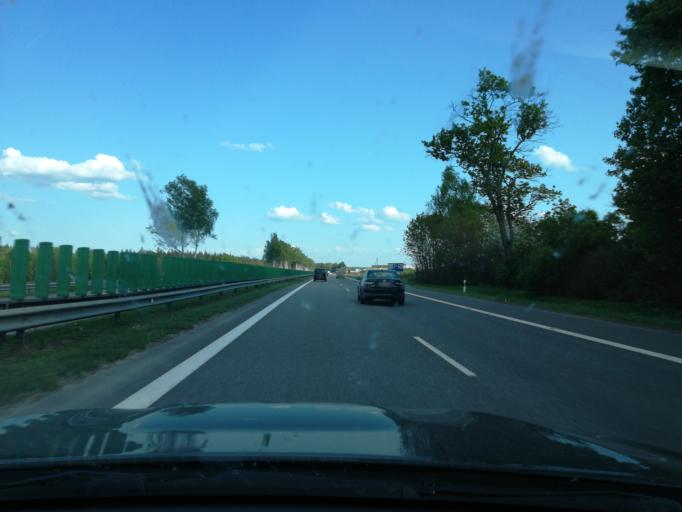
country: LT
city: Lentvaris
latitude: 54.7065
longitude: 24.9993
